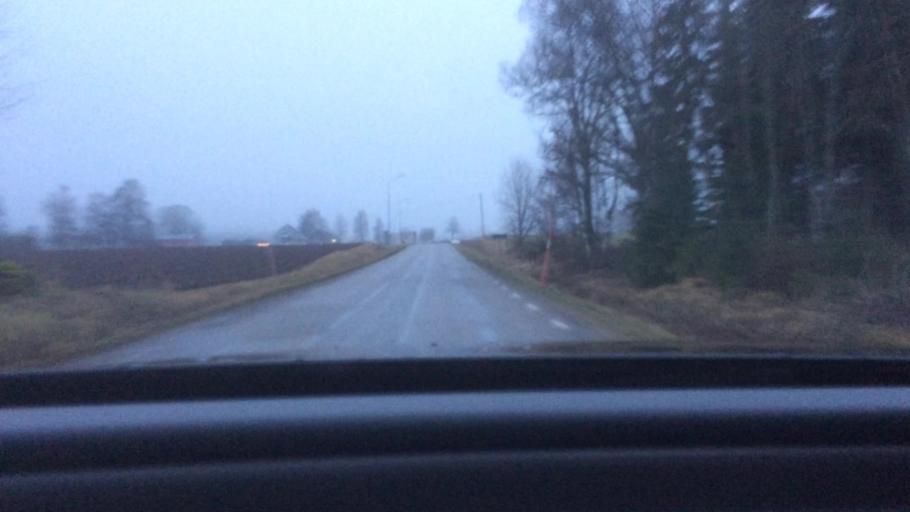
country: SE
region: Vaestra Goetaland
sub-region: Ulricehamns Kommun
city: Ulricehamn
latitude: 57.9475
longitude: 13.3859
